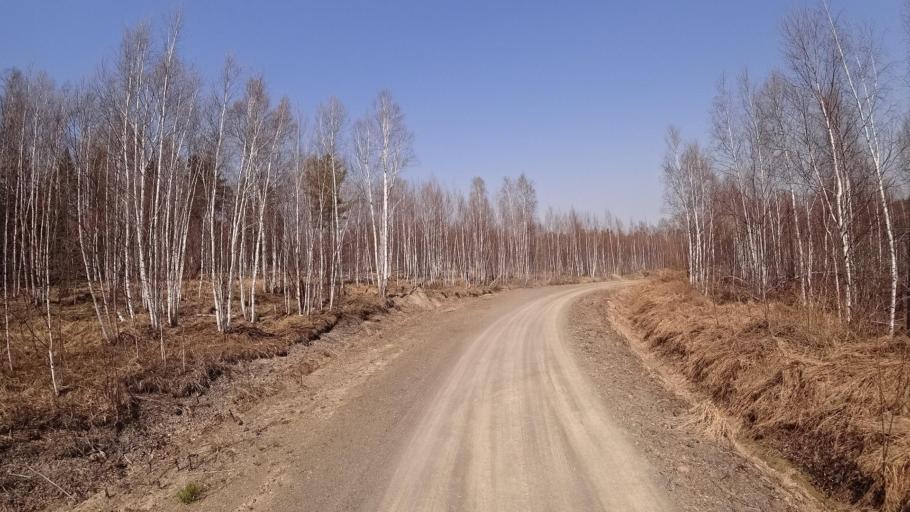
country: RU
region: Khabarovsk Krai
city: Selikhino
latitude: 50.6258
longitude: 137.4026
